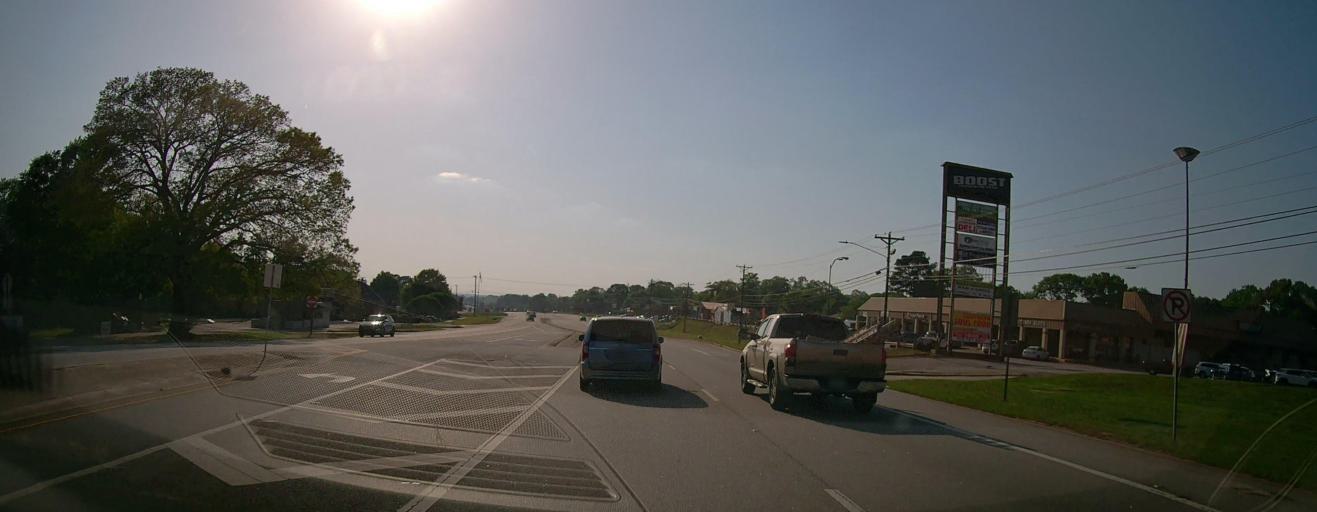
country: US
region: Georgia
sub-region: Newton County
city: Covington
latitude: 33.6018
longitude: -83.8408
